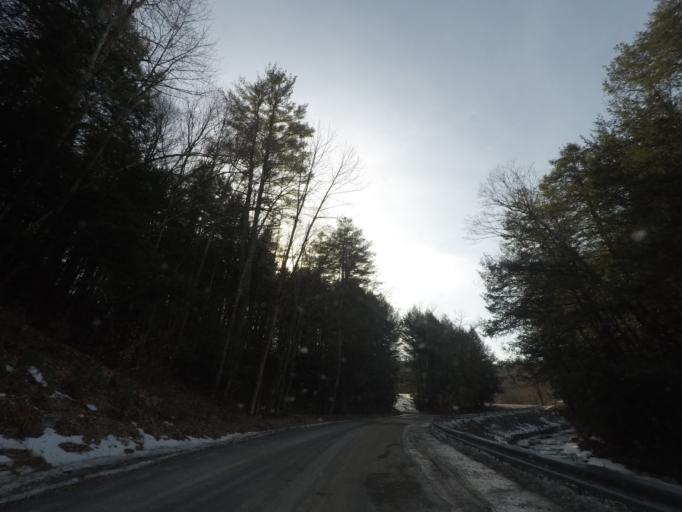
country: US
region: New York
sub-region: Rensselaer County
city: Hoosick Falls
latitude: 42.7625
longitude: -73.3585
